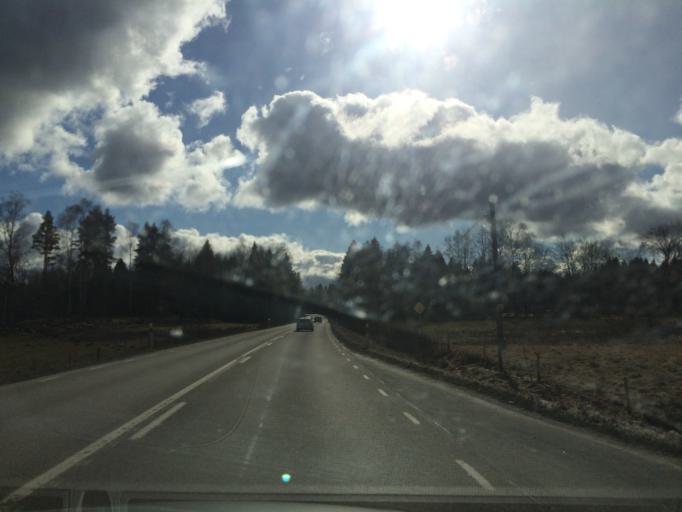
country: SE
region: Vaestra Goetaland
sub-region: Skara Kommun
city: Skara
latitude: 58.3275
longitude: 13.4367
